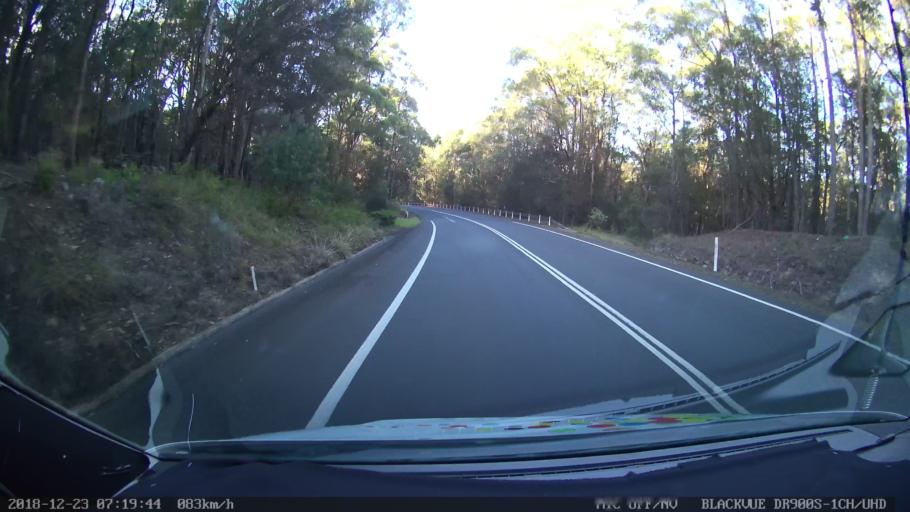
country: AU
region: New South Wales
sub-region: Bellingen
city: Dorrigo
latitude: -30.4841
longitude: 152.2827
